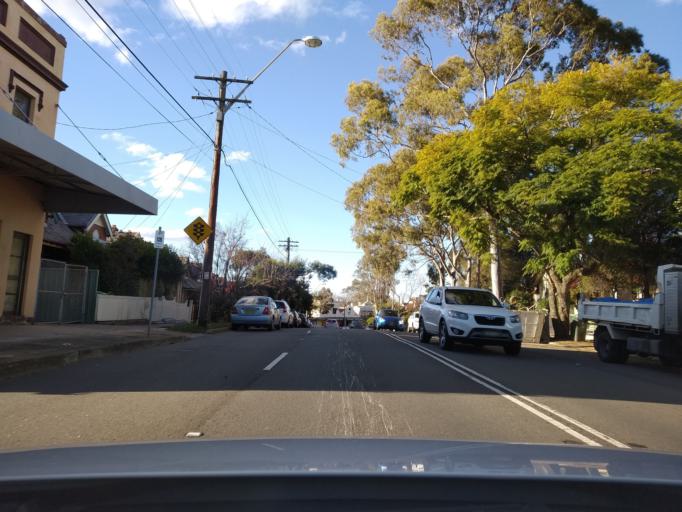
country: AU
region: New South Wales
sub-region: Ashfield
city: Summer Hill
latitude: -33.8964
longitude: 151.1374
